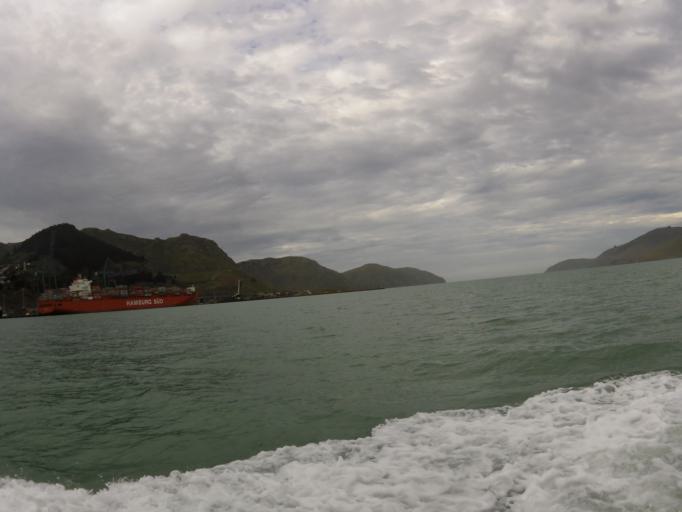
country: NZ
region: Canterbury
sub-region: Christchurch City
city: Christchurch
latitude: -43.6144
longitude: 172.7231
